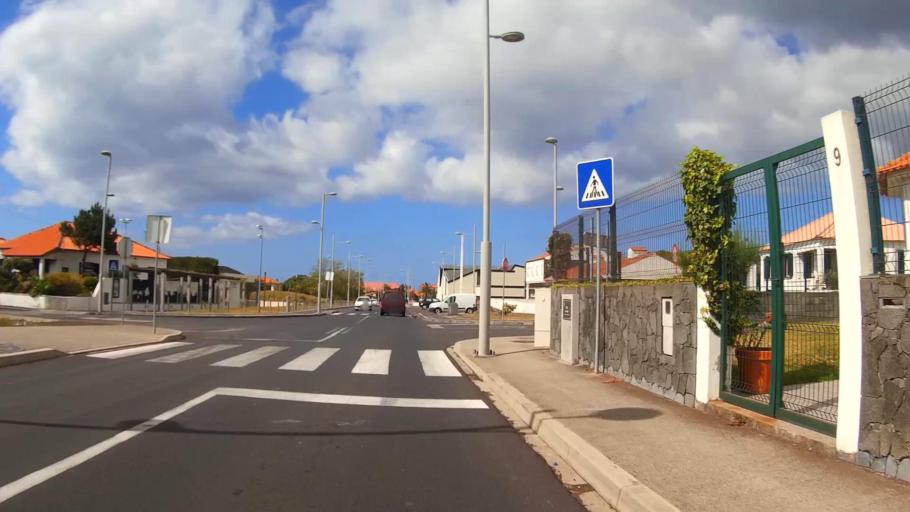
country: PT
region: Azores
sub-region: Madalena
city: Madalena
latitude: 38.5326
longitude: -28.5257
